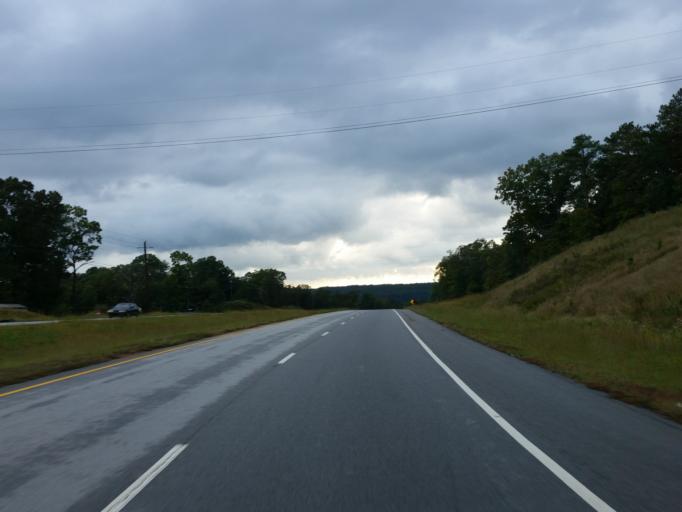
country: US
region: Georgia
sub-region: Bartow County
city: Emerson
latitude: 34.1176
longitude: -84.7702
